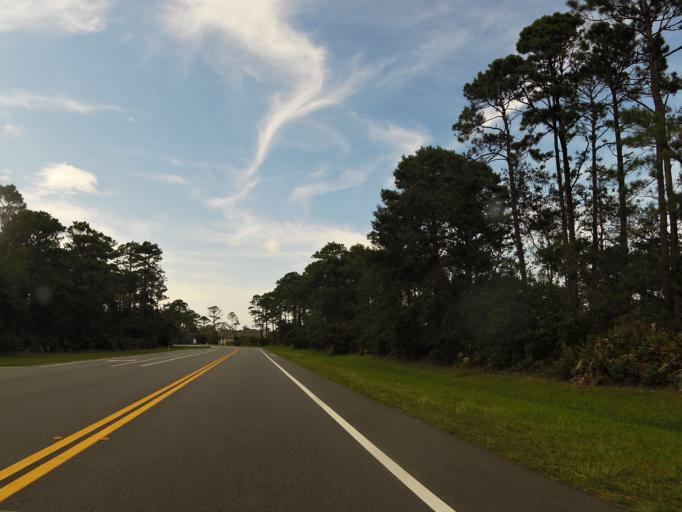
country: US
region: Florida
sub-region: Nassau County
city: Fernandina Beach
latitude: 30.6246
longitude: -81.4692
